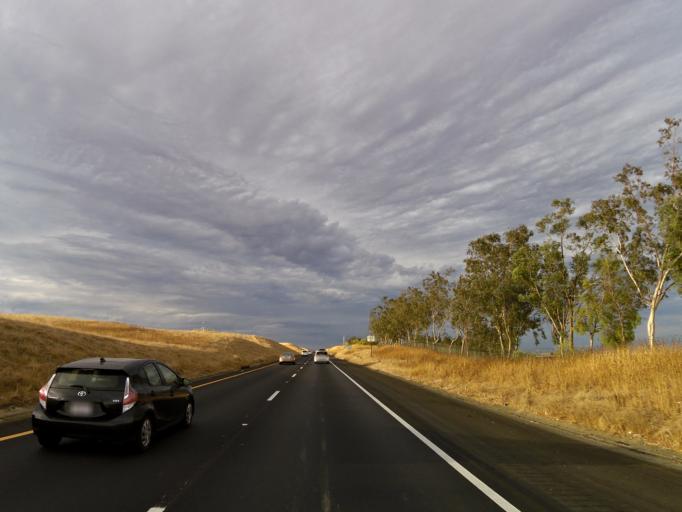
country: US
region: California
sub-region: Fresno County
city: Coalinga
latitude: 36.3031
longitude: -120.2752
